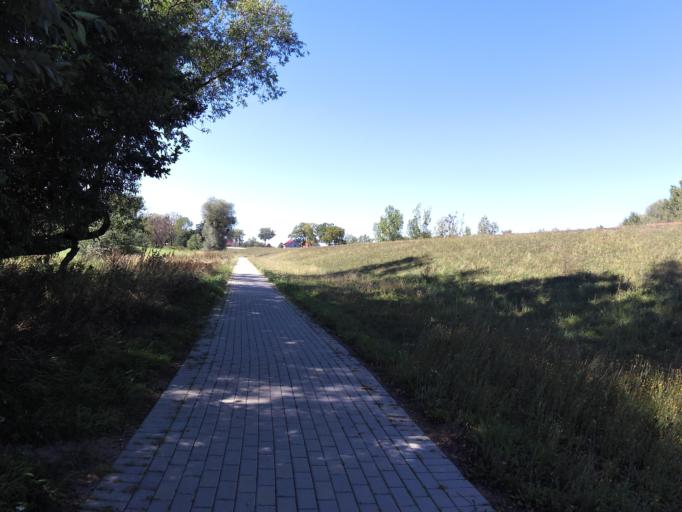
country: DE
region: Saxony-Anhalt
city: Elster
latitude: 51.8344
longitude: 12.7954
